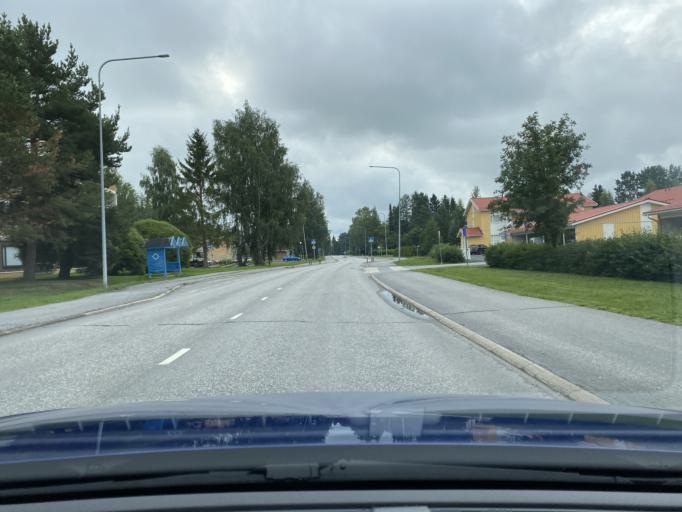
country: FI
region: Ostrobothnia
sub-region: Kyroenmaa
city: Laihia
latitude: 62.9744
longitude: 22.0165
